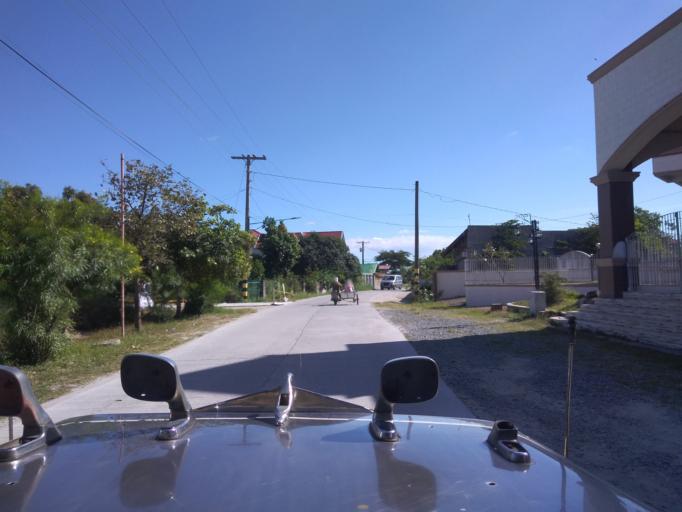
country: PH
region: Central Luzon
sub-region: Province of Pampanga
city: Magliman
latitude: 15.0257
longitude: 120.6367
